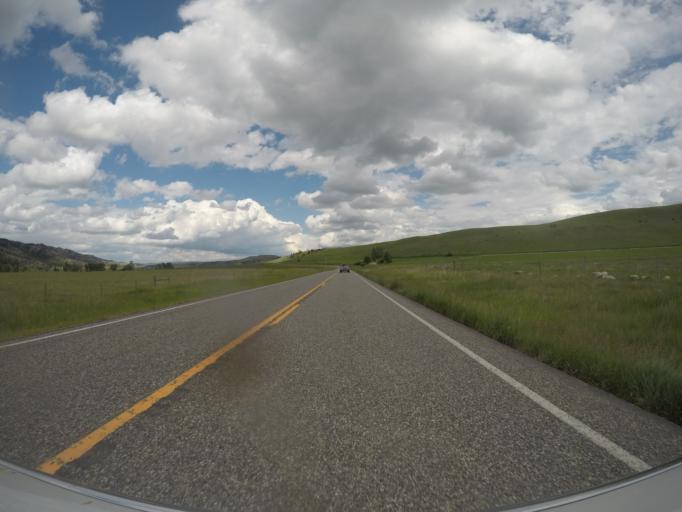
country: US
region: Montana
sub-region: Sweet Grass County
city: Big Timber
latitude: 45.6900
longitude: -110.0527
